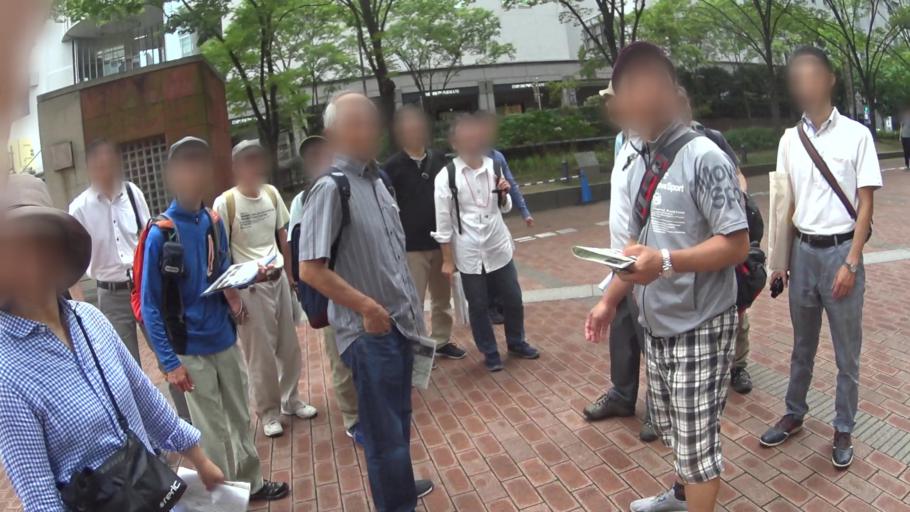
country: JP
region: Osaka
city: Osaka-shi
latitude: 34.6995
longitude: 135.4930
